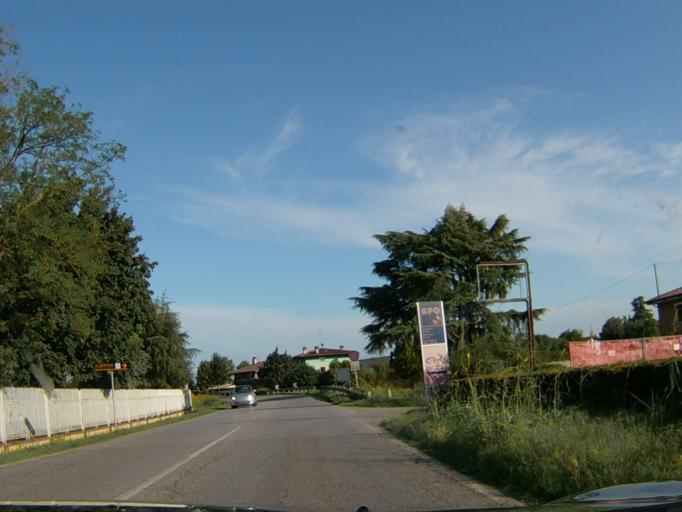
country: IT
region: Lombardy
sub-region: Provincia di Brescia
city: Molinetto
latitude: 45.4872
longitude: 10.3691
